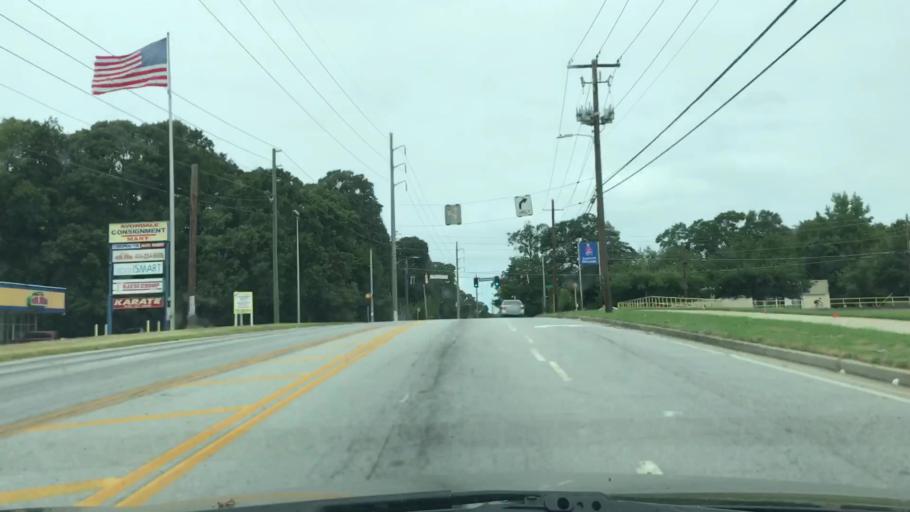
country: US
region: Georgia
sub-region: DeKalb County
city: Belvedere Park
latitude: 33.7560
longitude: -84.2697
